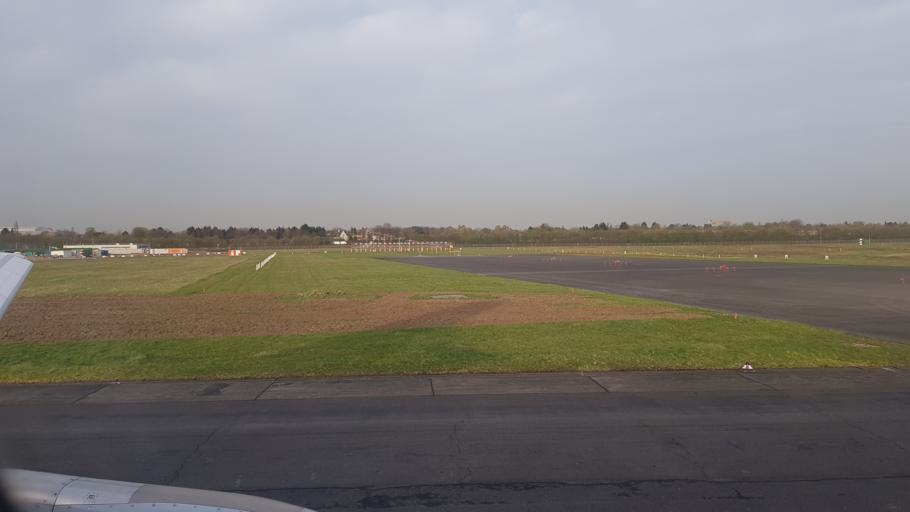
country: DE
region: North Rhine-Westphalia
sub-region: Regierungsbezirk Dusseldorf
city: Dusseldorf
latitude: 51.2793
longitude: 6.7527
